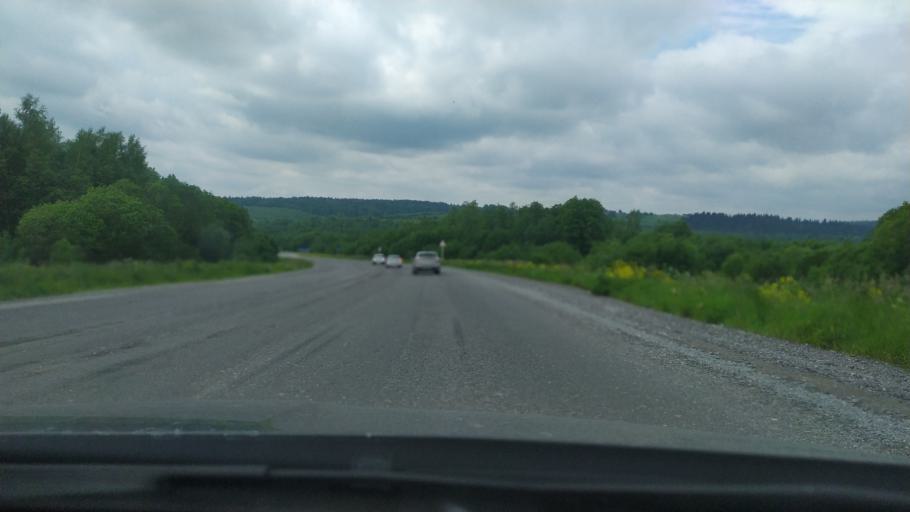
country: RU
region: Perm
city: Kalino
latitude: 58.2684
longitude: 57.3496
